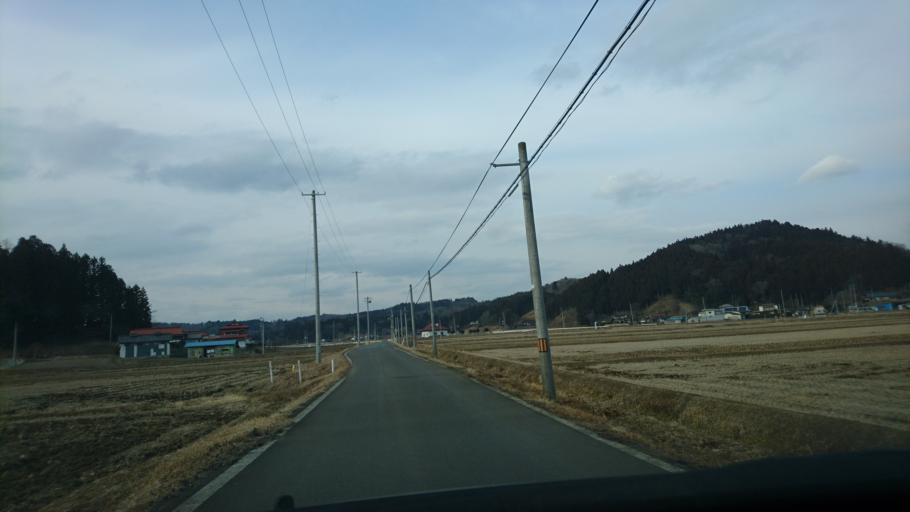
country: JP
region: Iwate
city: Ichinoseki
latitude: 38.8309
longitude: 141.2473
